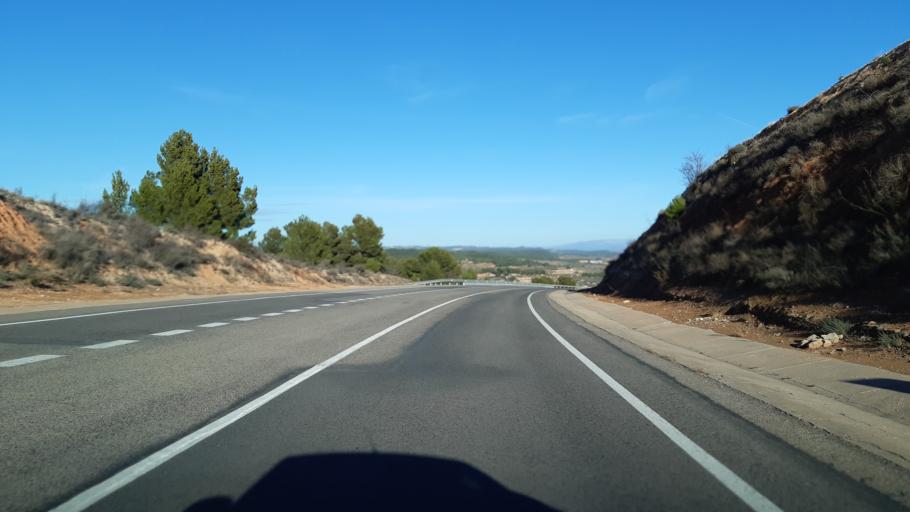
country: ES
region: Catalonia
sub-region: Provincia de Tarragona
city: Bot
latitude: 41.0536
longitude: 0.3915
